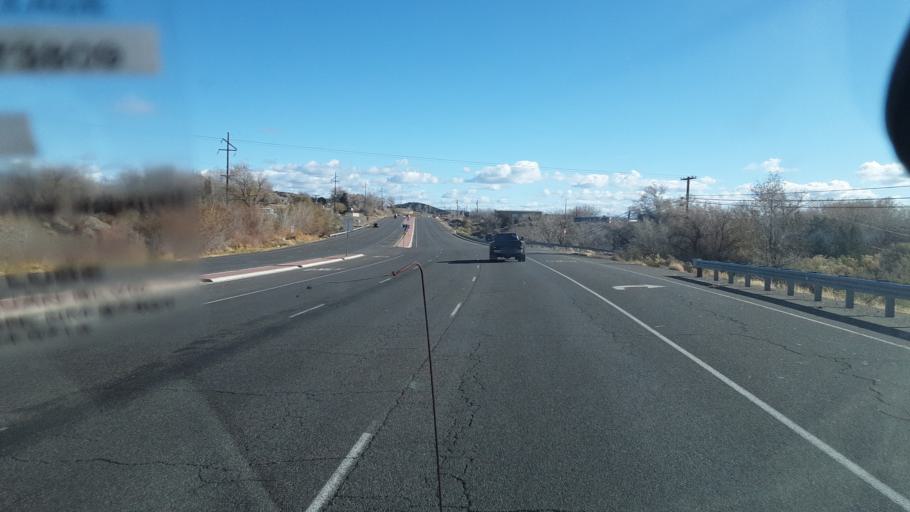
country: US
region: New Mexico
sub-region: San Juan County
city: Lee Acres
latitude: 36.7009
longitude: -108.0365
